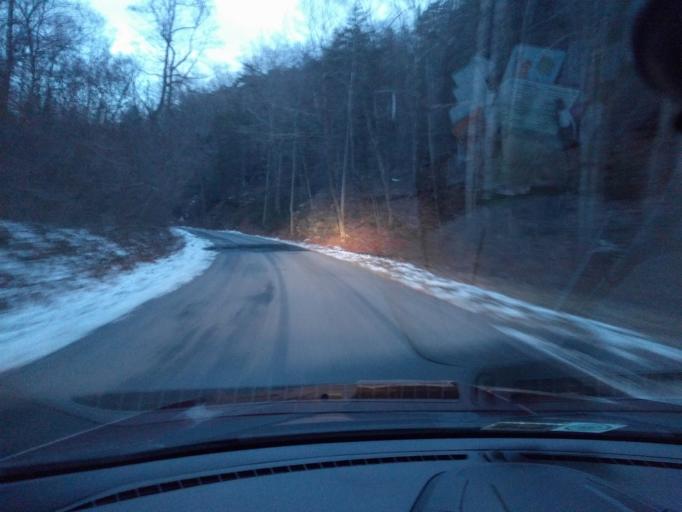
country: US
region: Virginia
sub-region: Alleghany County
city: Clifton Forge
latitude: 37.8582
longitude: -79.8675
